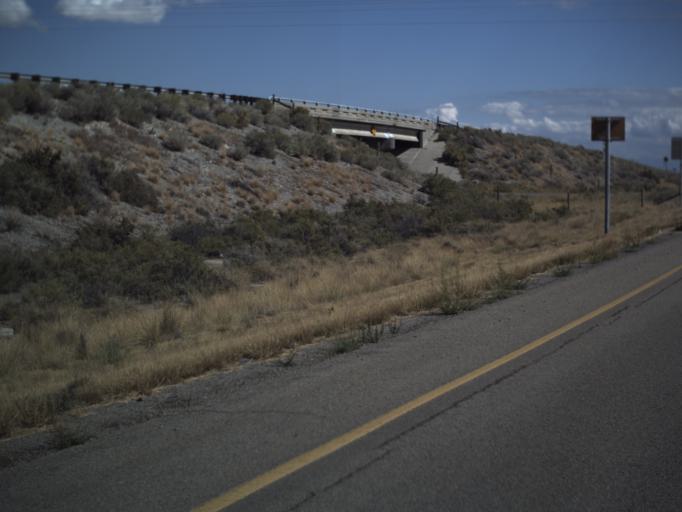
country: US
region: Utah
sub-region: Tooele County
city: Grantsville
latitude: 40.7454
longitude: -112.6543
